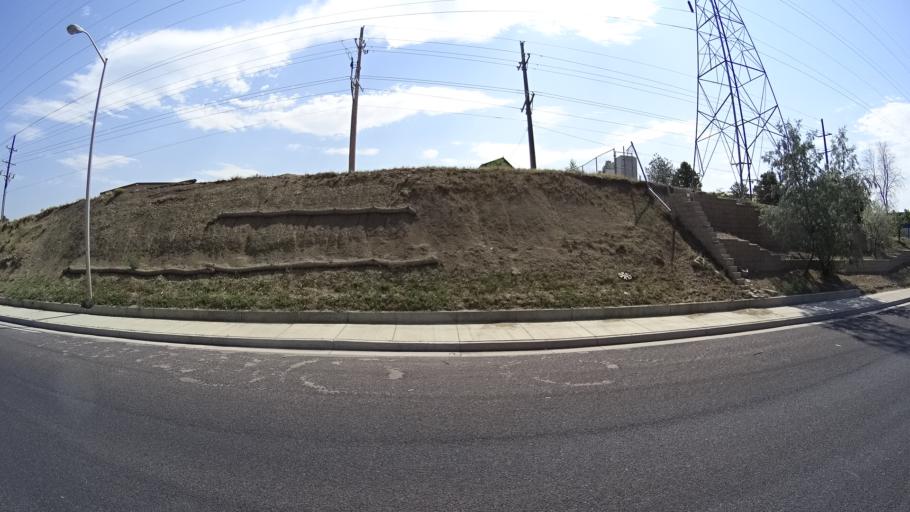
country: US
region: Colorado
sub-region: El Paso County
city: Stratmoor
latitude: 38.8217
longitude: -104.7574
